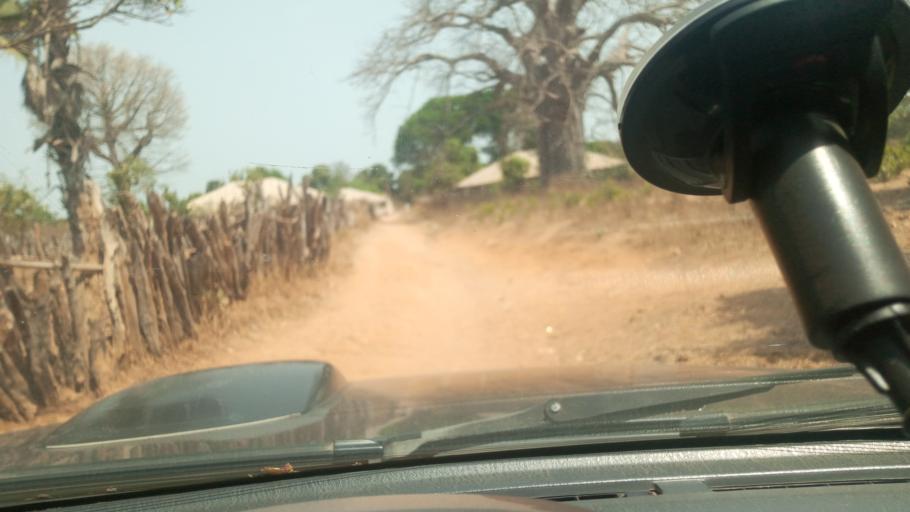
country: SN
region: Sedhiou
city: Sedhiou
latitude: 12.4410
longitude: -15.6158
